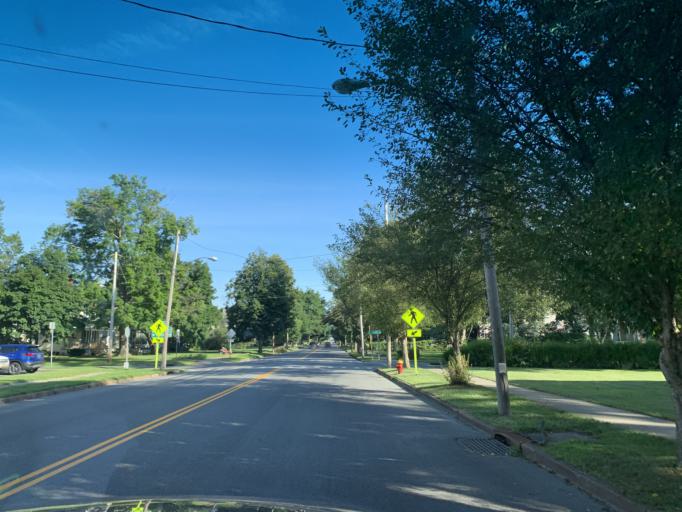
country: US
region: New York
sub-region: Madison County
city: Oneida
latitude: 43.0853
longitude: -75.6460
